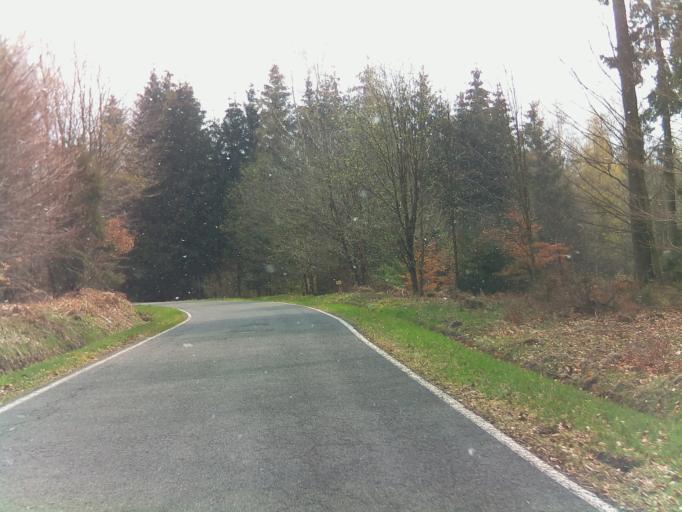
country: DE
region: Rheinland-Pfalz
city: Schauren
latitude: 49.8236
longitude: 7.2573
